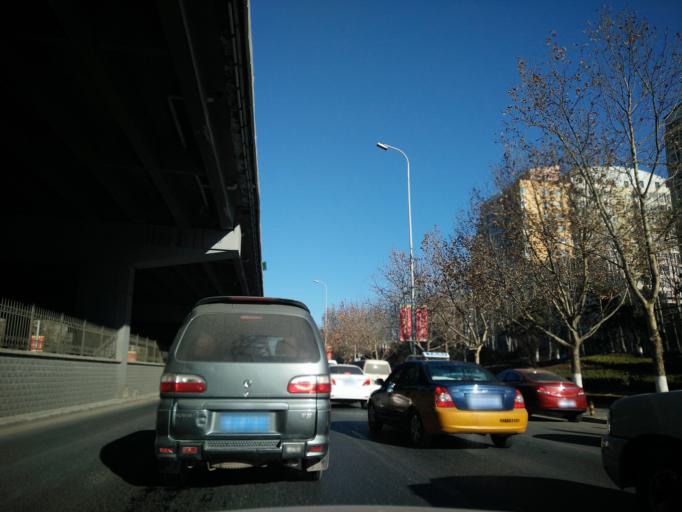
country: CN
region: Beijing
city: Xingfeng
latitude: 39.7374
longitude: 116.3394
